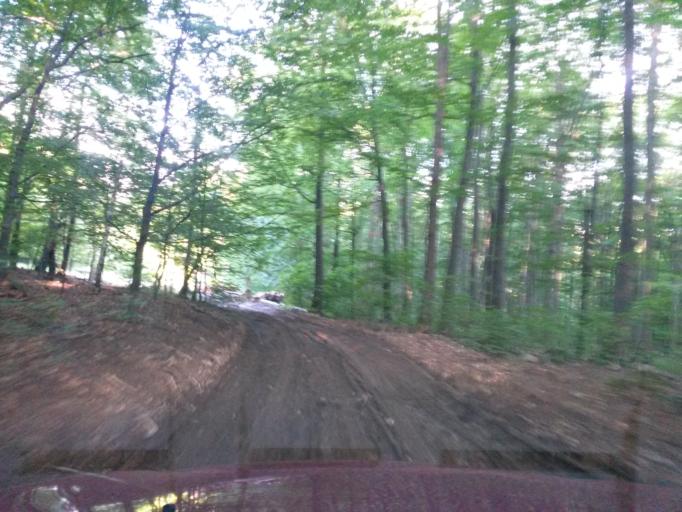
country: SK
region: Kosicky
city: Moldava nad Bodvou
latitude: 48.7296
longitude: 21.0515
